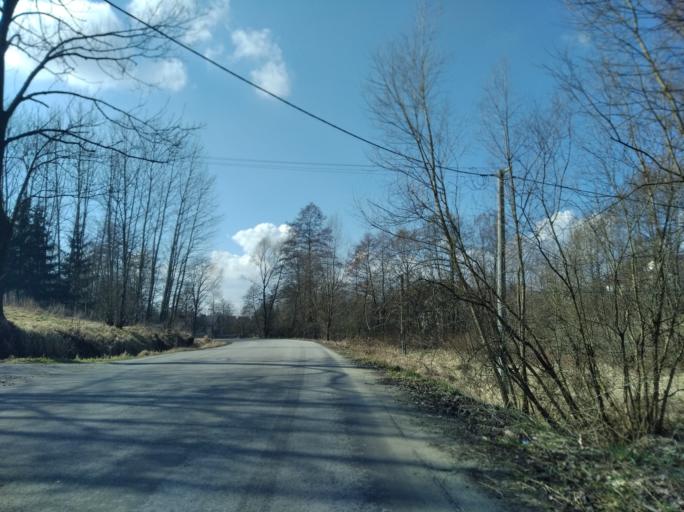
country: PL
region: Subcarpathian Voivodeship
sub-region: Powiat debicki
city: Brzostek
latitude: 49.8852
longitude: 21.4573
